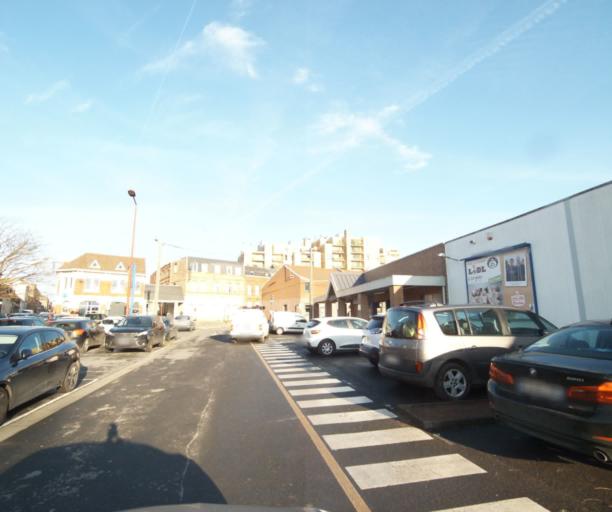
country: FR
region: Nord-Pas-de-Calais
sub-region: Departement du Nord
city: Valenciennes
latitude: 50.3507
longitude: 3.5403
